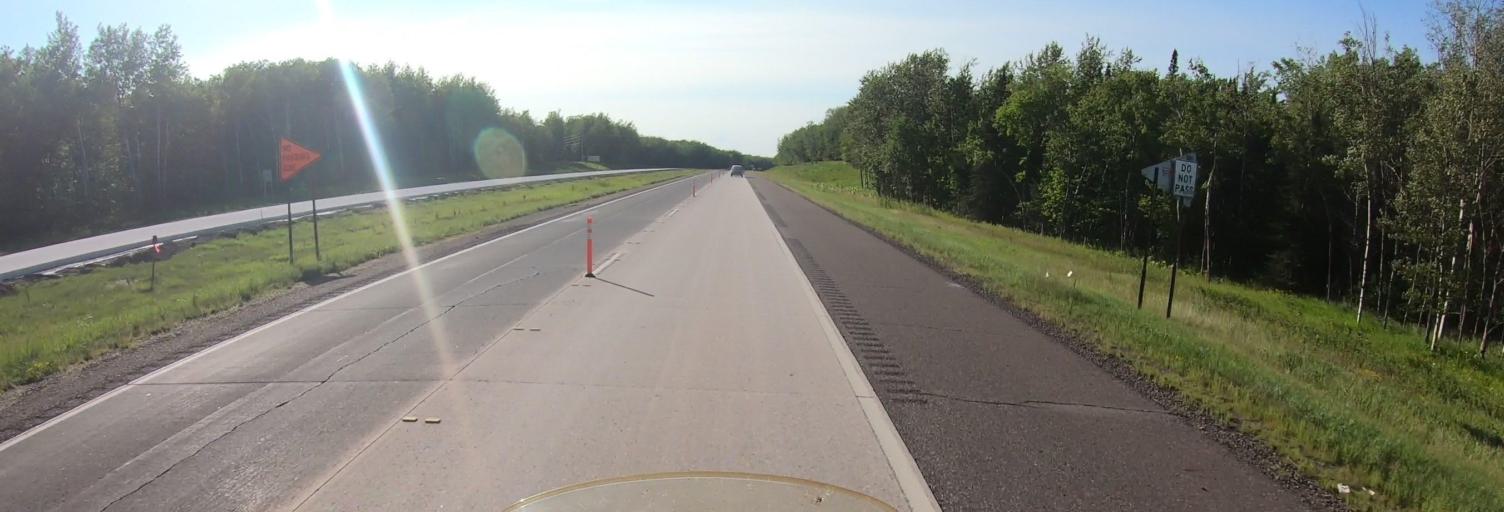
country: US
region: Minnesota
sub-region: Saint Louis County
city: Hermantown
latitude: 46.8570
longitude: -92.3122
